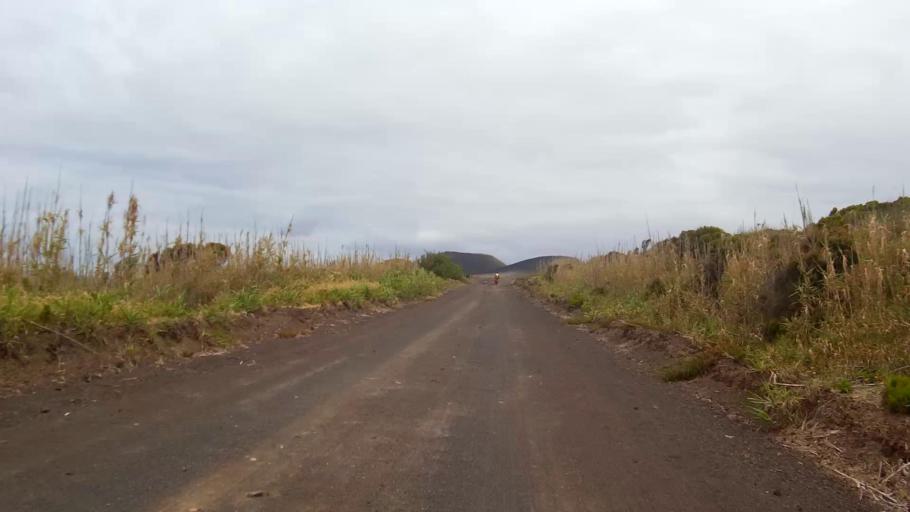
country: PT
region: Azores
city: Ribeira Grande
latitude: 38.5877
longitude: -28.8216
